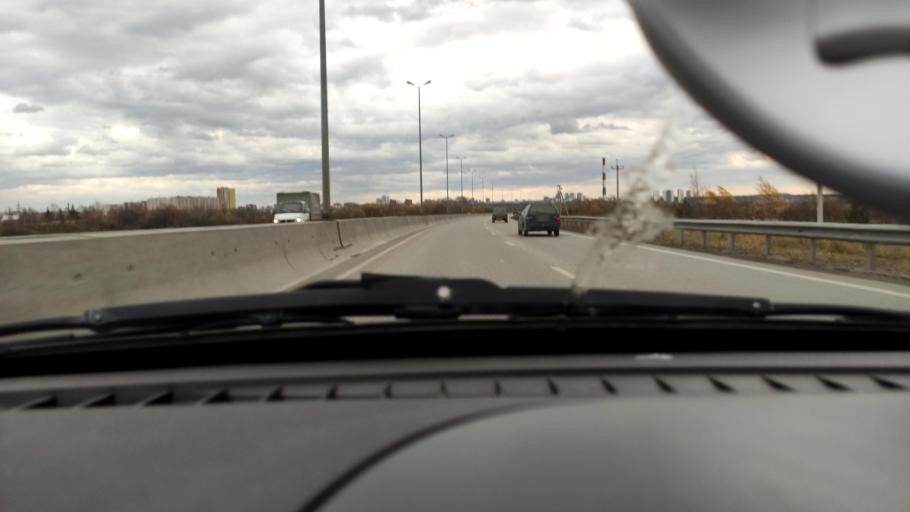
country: RU
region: Perm
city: Kondratovo
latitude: 58.0023
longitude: 56.0867
